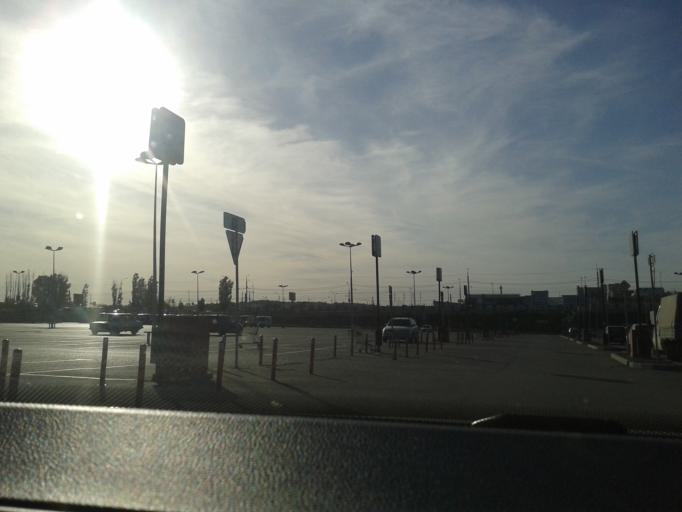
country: RU
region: Volgograd
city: Volgograd
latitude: 48.6369
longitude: 44.4331
